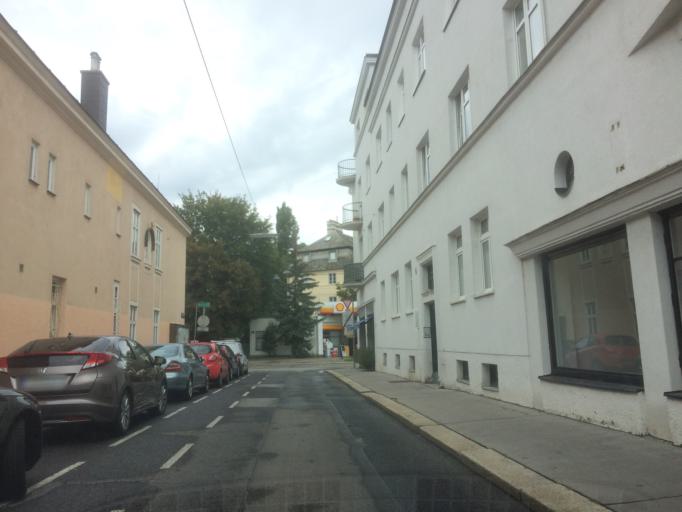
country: AT
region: Lower Austria
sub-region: Politischer Bezirk Modling
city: Perchtoldsdorf
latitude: 48.1850
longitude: 16.2966
